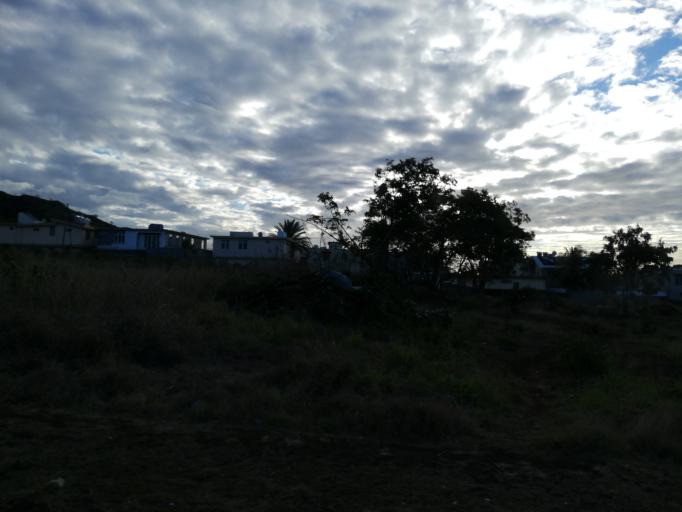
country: MU
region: Moka
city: Pailles
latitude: -20.2023
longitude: 57.4697
